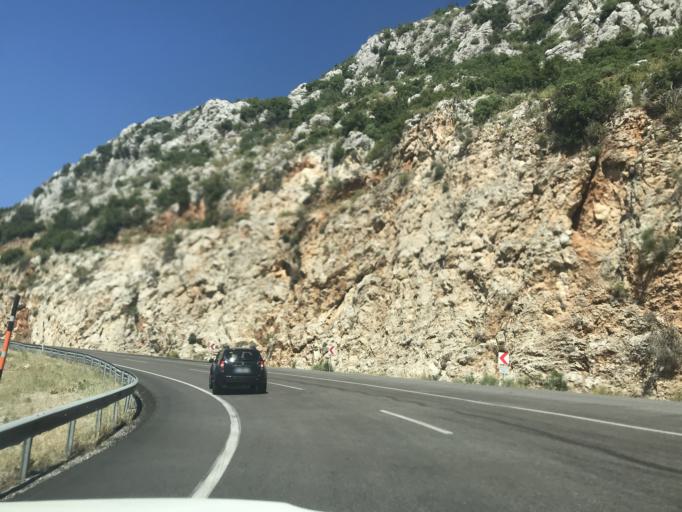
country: TR
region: Antalya
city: Dagbeli
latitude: 37.1646
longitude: 30.5099
